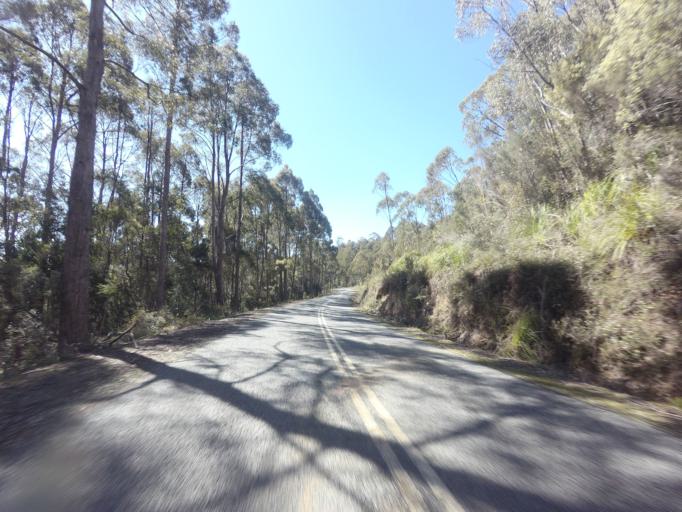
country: AU
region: Tasmania
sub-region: Huon Valley
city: Geeveston
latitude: -42.7833
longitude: 146.3993
